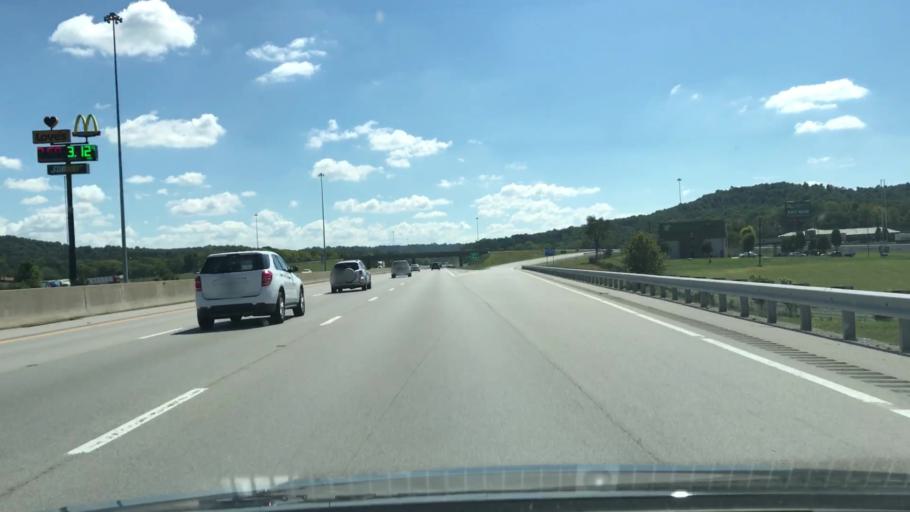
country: US
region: Kentucky
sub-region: Hart County
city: Horse Cave
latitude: 37.2060
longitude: -85.9375
